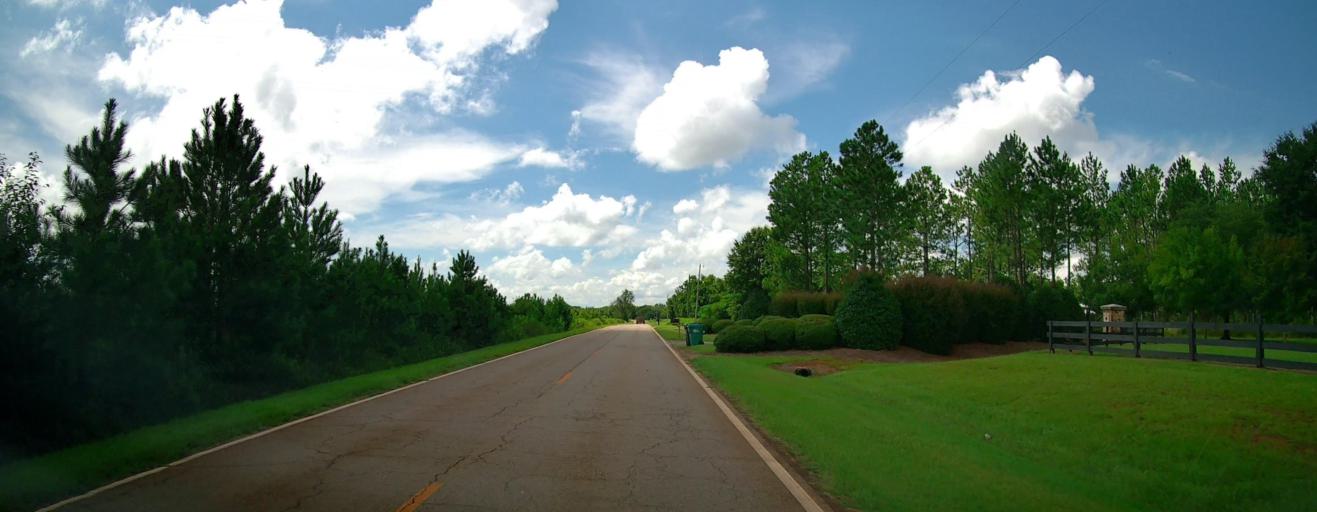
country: US
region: Georgia
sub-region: Houston County
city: Perry
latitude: 32.5220
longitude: -83.7612
